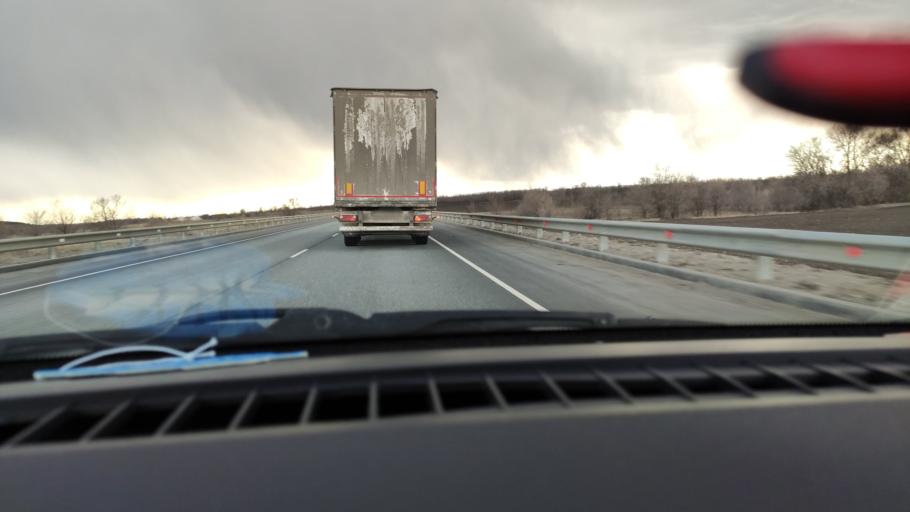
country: RU
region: Saratov
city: Yelshanka
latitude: 51.8495
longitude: 46.4874
